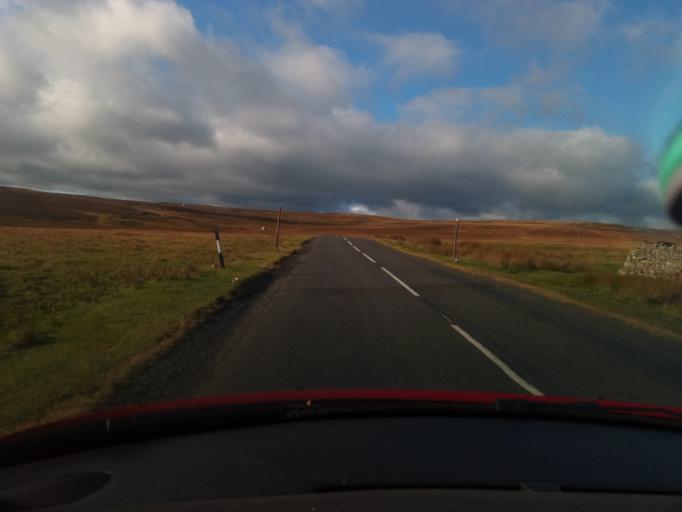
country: GB
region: Scotland
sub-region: The Scottish Borders
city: Lauder
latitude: 55.7109
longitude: -2.7899
